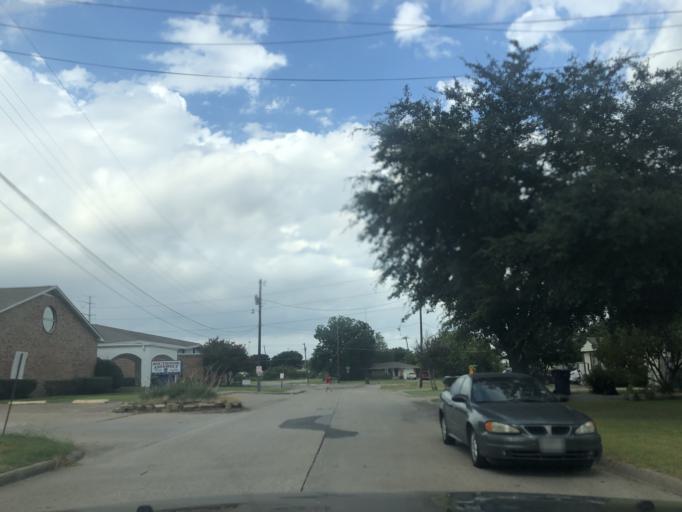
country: US
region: Texas
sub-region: Dallas County
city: Garland
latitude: 32.8829
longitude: -96.6547
